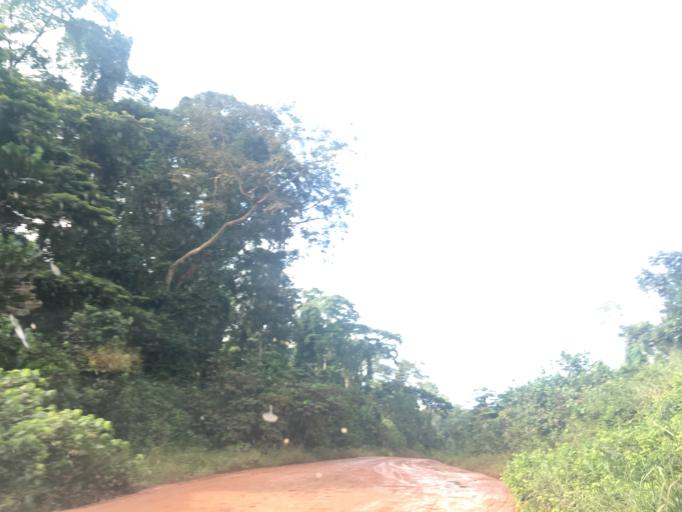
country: GH
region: Western
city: Wassa-Akropong
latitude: 5.9650
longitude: -2.4232
